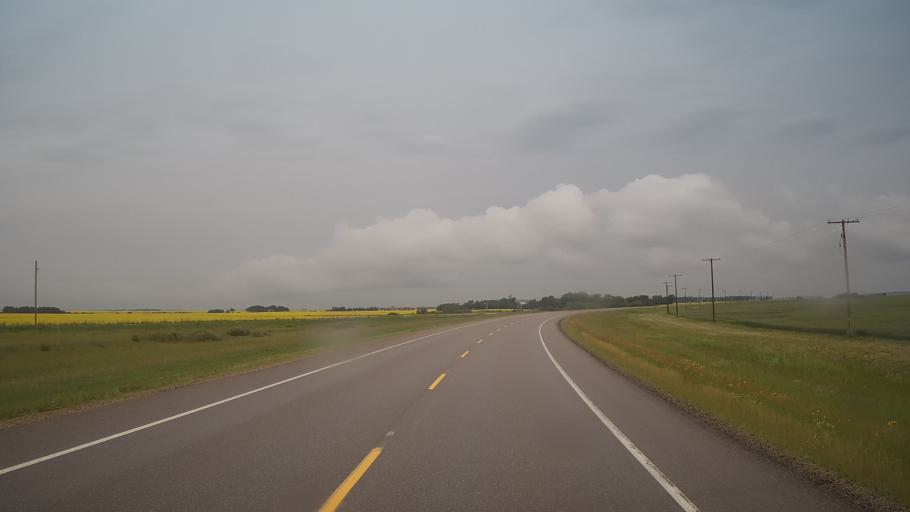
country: CA
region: Saskatchewan
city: Wilkie
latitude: 52.3303
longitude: -108.7121
